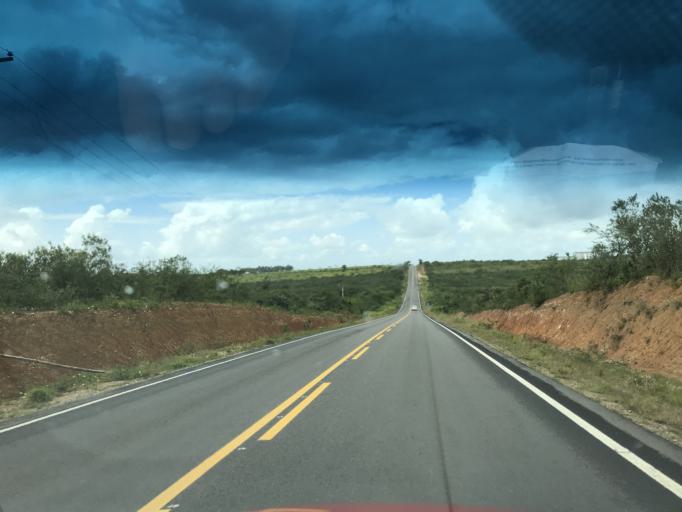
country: BR
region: Bahia
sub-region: Conceicao Do Almeida
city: Conceicao do Almeida
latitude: -12.6730
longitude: -39.2697
